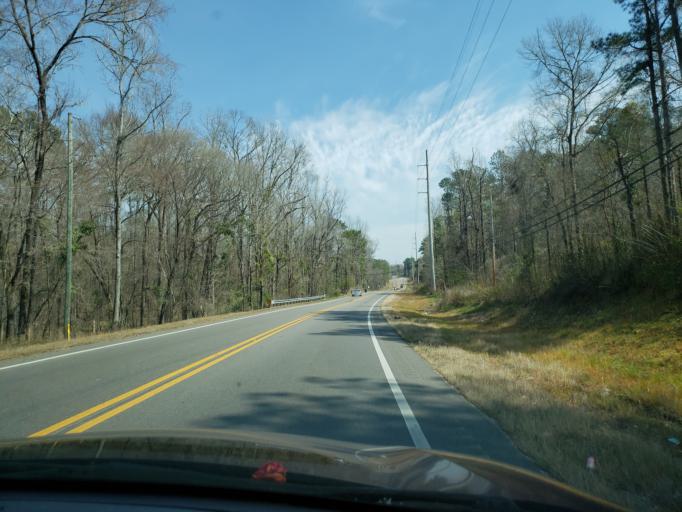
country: US
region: Alabama
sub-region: Elmore County
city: Wetumpka
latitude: 32.5532
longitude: -86.1696
